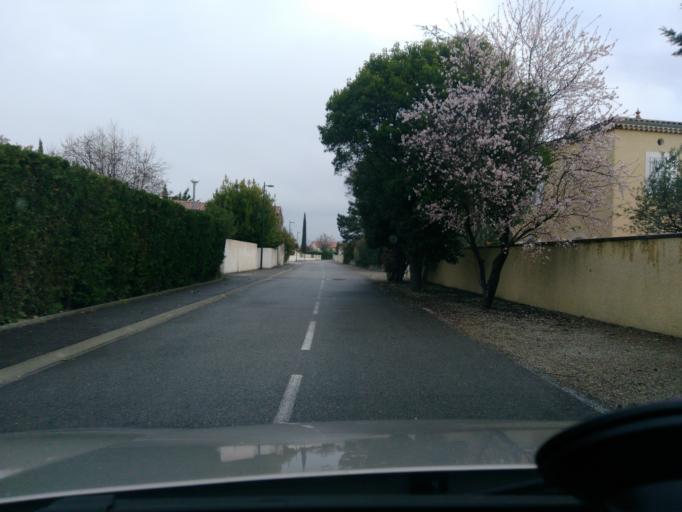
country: FR
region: Rhone-Alpes
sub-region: Departement de la Drome
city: Montelimar
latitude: 44.5340
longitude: 4.7556
